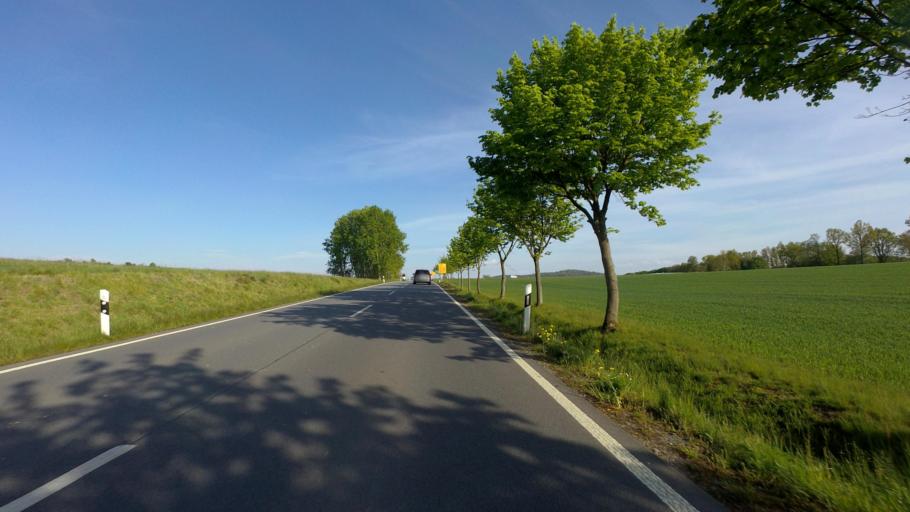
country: DE
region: Saxony
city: Stolpen
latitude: 51.0389
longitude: 14.1336
